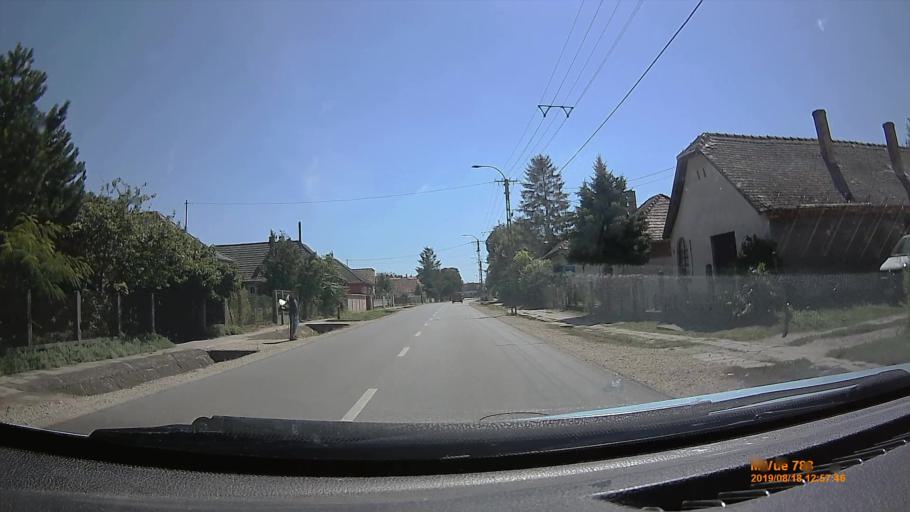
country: HU
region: Fejer
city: Sarkeresztur
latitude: 47.0105
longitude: 18.5454
